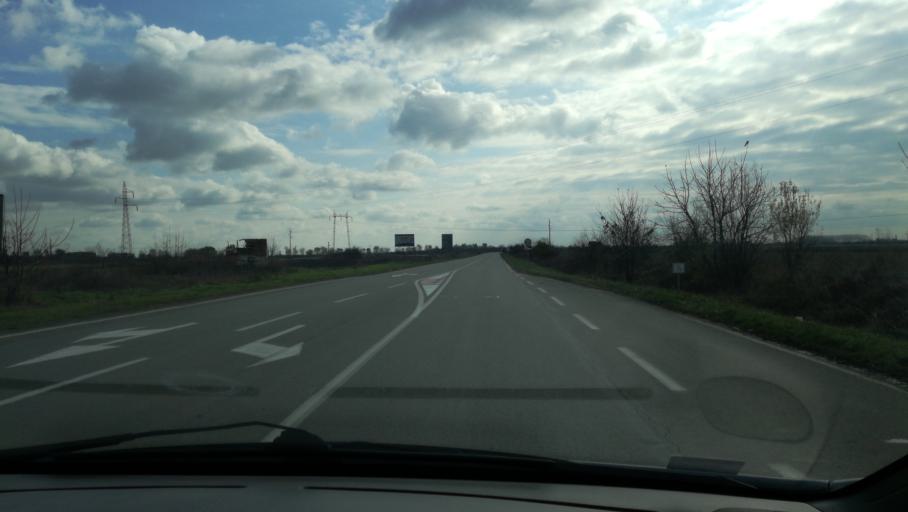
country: RS
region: Autonomna Pokrajina Vojvodina
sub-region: Severnobanatski Okrug
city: Kikinda
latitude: 45.8058
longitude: 20.4349
